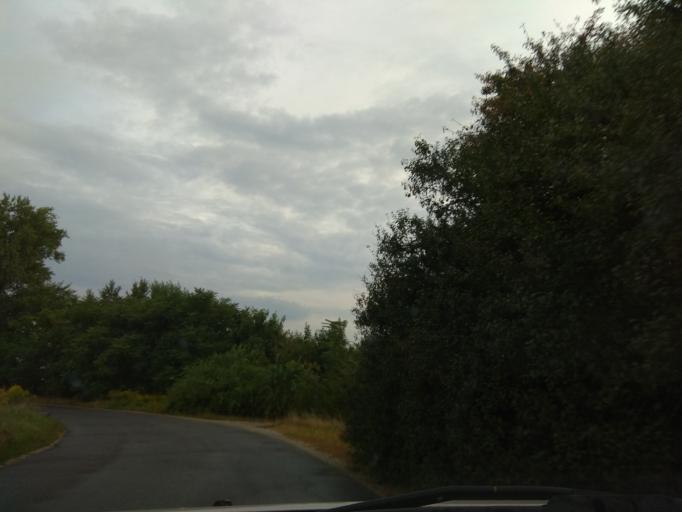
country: HU
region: Borsod-Abauj-Zemplen
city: Felsozsolca
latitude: 48.0961
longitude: 20.8316
